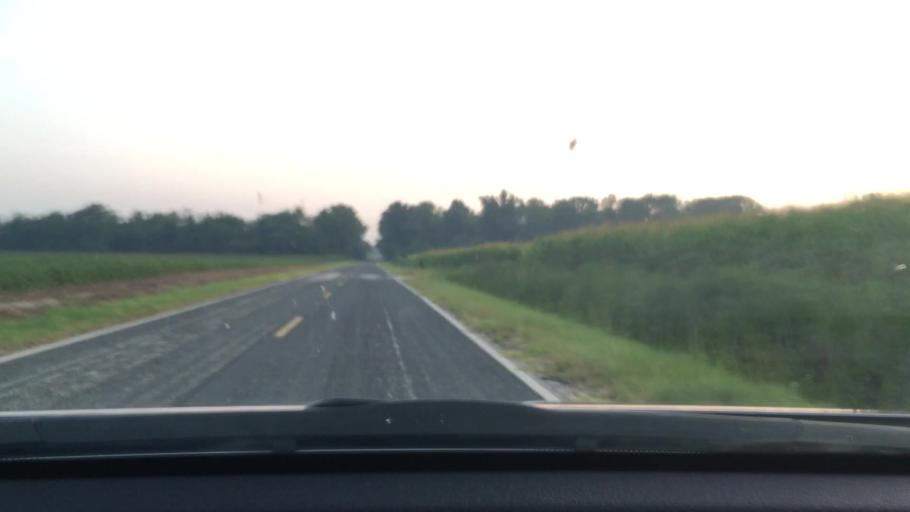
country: US
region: South Carolina
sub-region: Lee County
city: Bishopville
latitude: 34.2537
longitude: -80.1344
